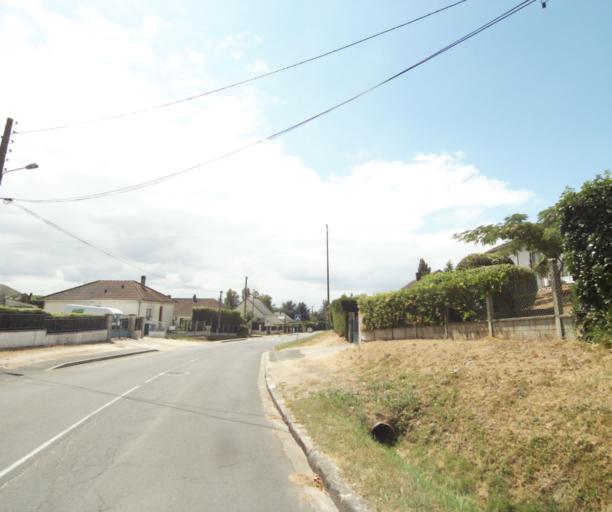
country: FR
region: Centre
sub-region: Departement du Loiret
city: Mardie
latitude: 47.8854
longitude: 2.0553
